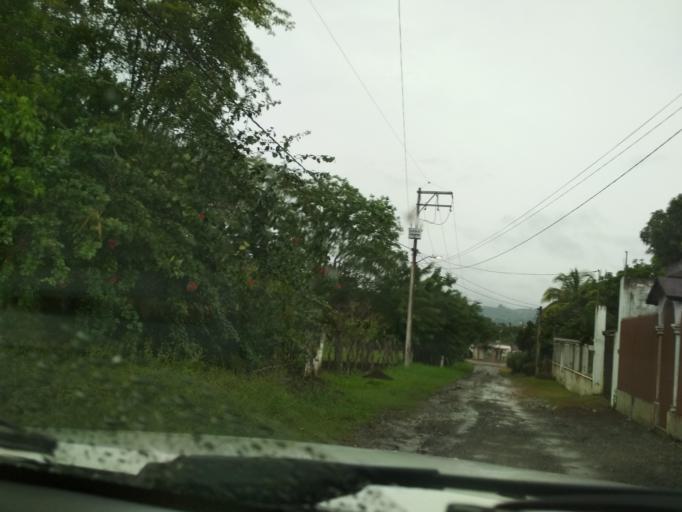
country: MX
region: Veracruz
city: Santiago Tuxtla
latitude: 18.4583
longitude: -95.3073
